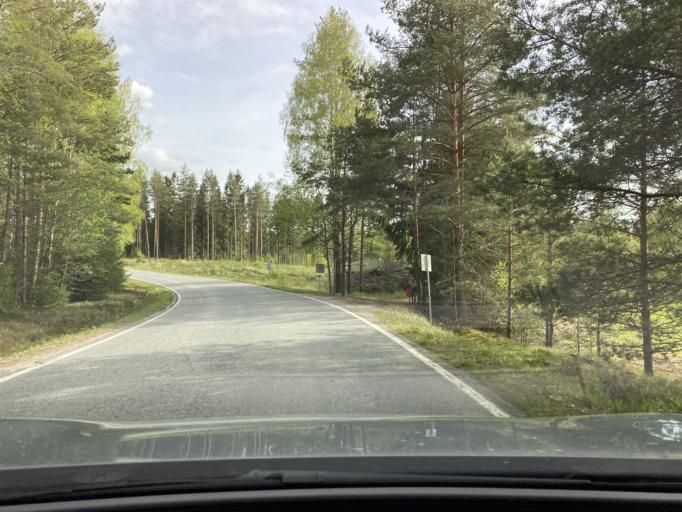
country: FI
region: Varsinais-Suomi
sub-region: Salo
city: Kiikala
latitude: 60.5145
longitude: 23.5309
